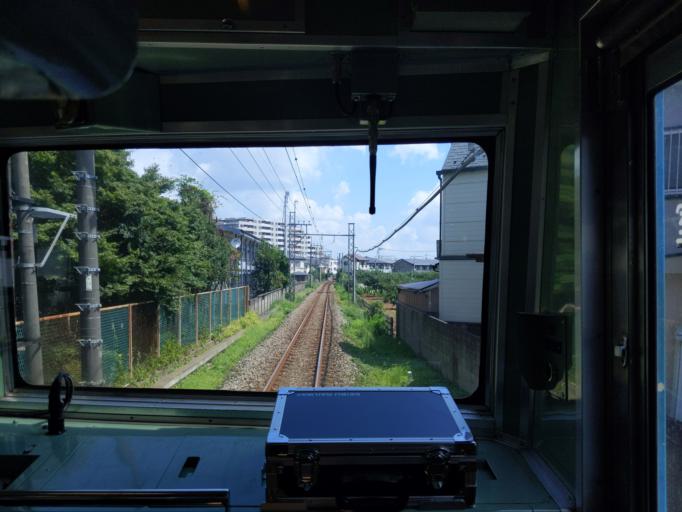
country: JP
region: Tokyo
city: Kamirenjaku
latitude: 35.7002
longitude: 139.5333
